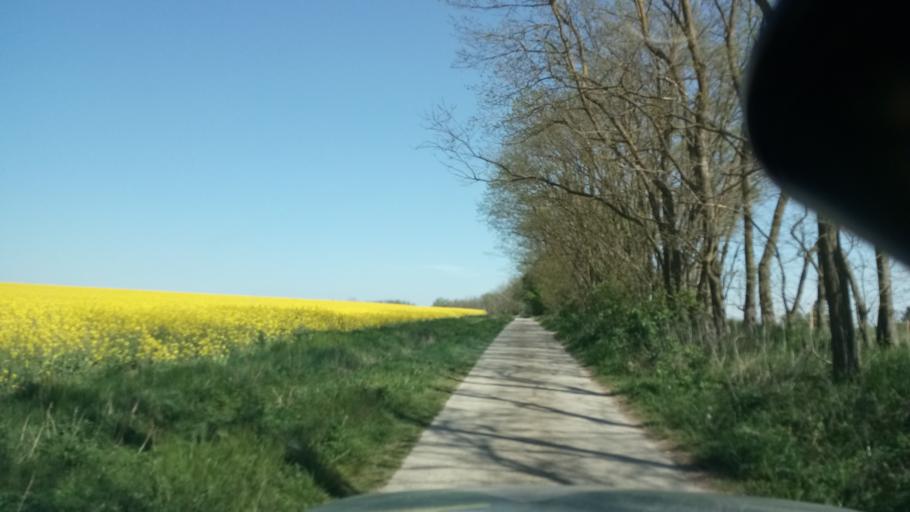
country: HU
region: Zala
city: Sarmellek
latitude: 46.7038
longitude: 17.0909
